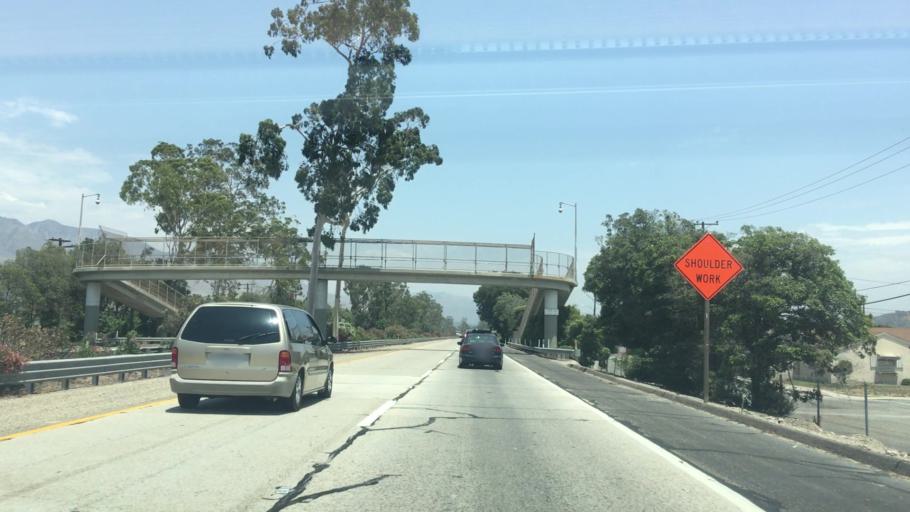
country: US
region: California
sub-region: Ventura County
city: Santa Paula
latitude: 34.3389
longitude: -119.0798
